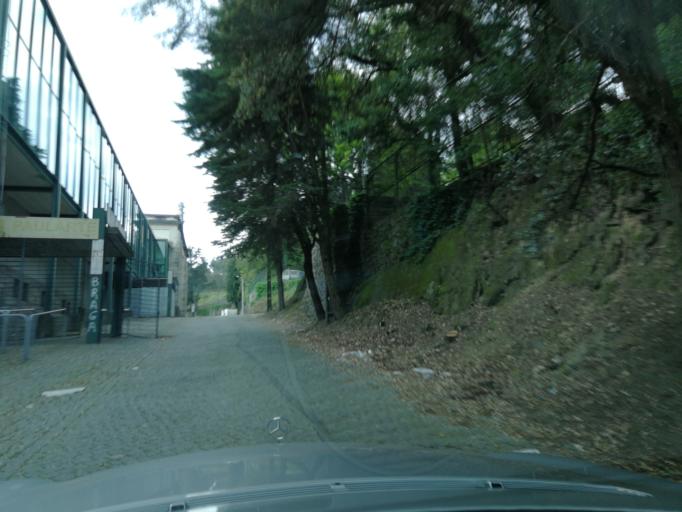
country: PT
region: Braga
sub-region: Braga
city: Braga
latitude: 41.5394
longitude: -8.4219
